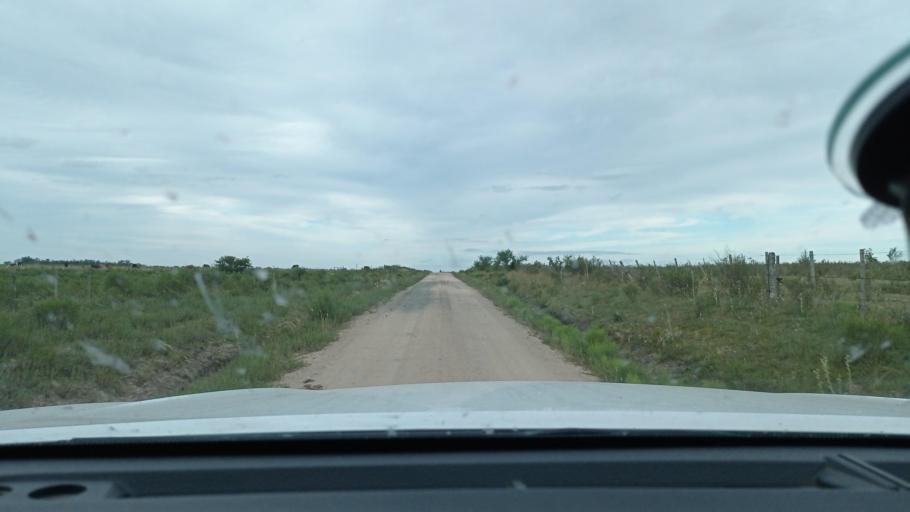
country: UY
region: Florida
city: Casupa
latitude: -34.1452
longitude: -55.7906
